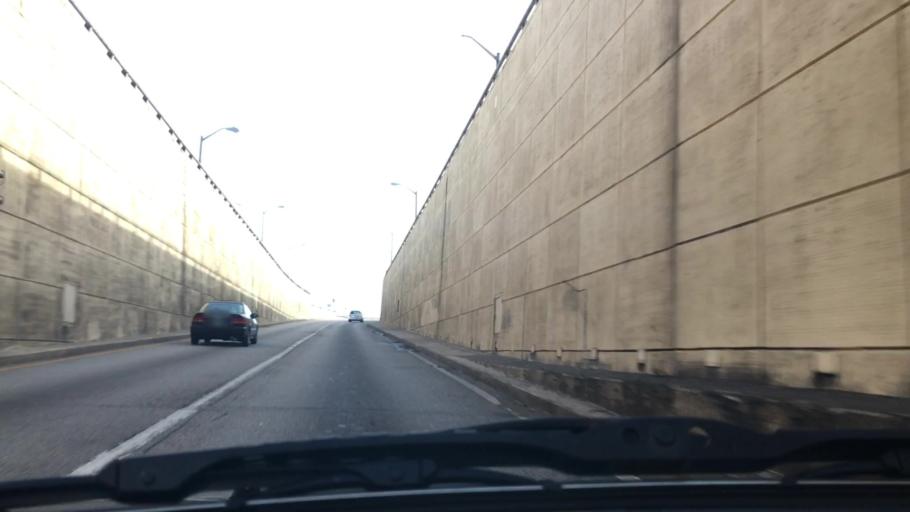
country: US
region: Virginia
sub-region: City of Hampton
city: East Hampton
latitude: 36.9842
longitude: -76.3031
